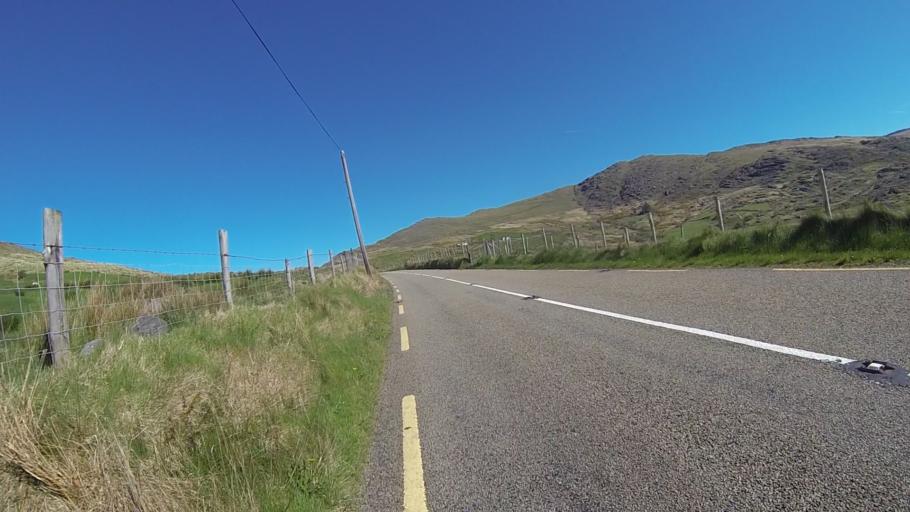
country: IE
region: Munster
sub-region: Ciarrai
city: Kenmare
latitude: 51.7790
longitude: -9.7290
